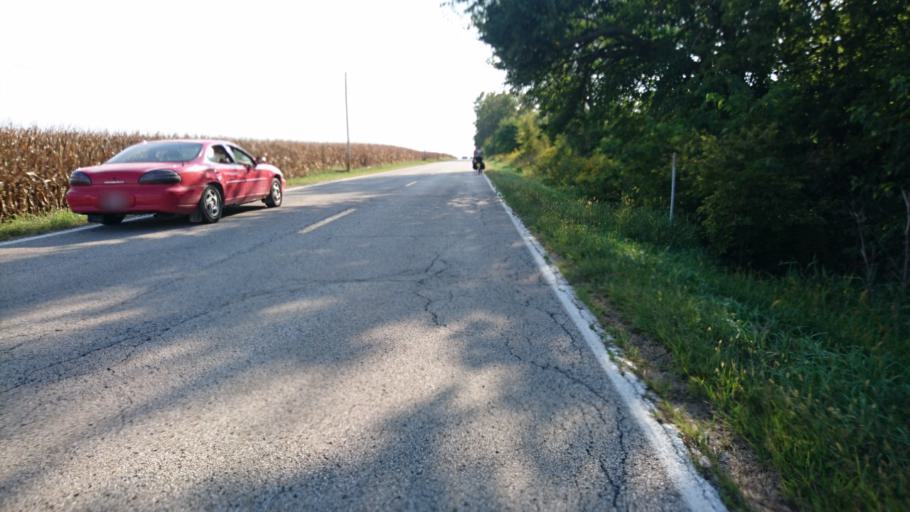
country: US
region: Illinois
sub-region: Logan County
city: Atlanta
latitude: 40.3092
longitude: -89.1757
